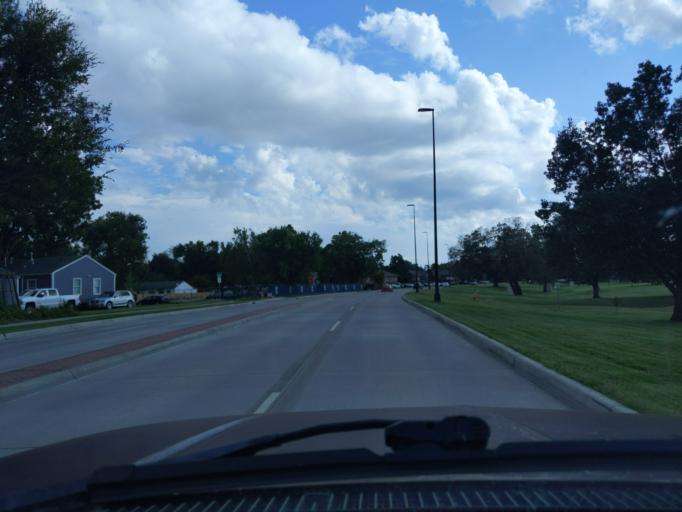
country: US
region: Oklahoma
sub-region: Tulsa County
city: Tulsa
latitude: 36.1089
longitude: -95.9831
